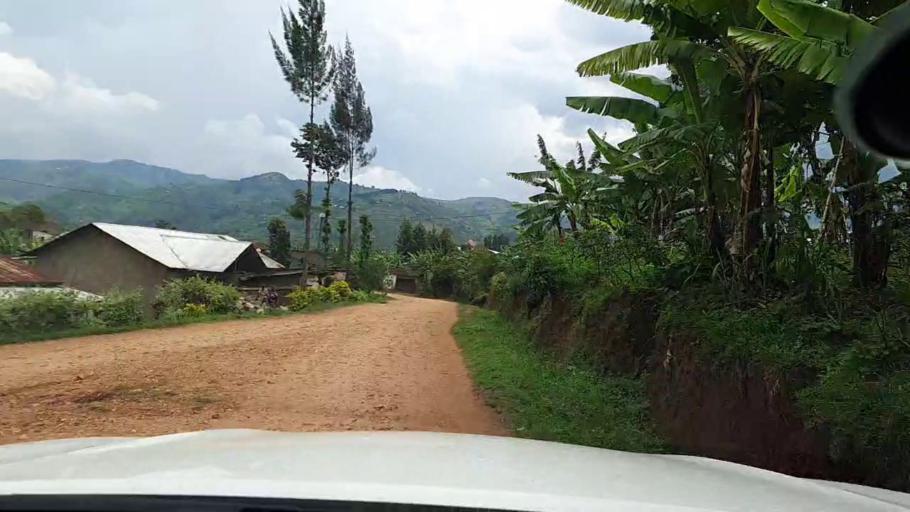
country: RW
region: Western Province
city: Kibuye
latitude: -2.0719
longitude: 29.4277
